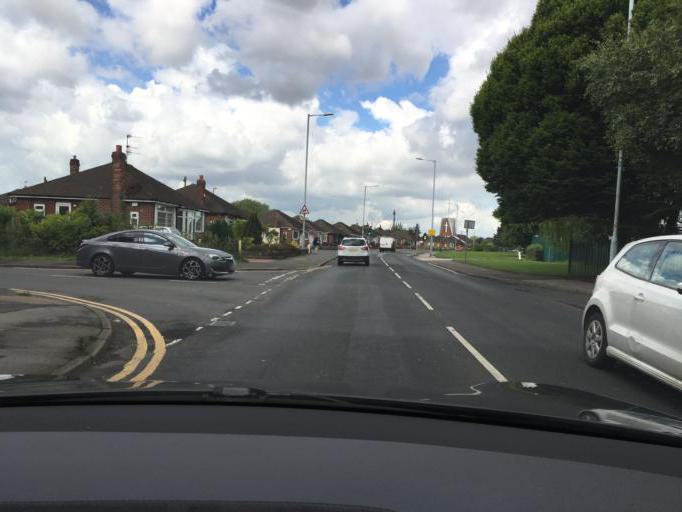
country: GB
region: England
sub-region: Borough of Stockport
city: Cheadle Hulme
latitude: 53.3880
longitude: -2.1875
